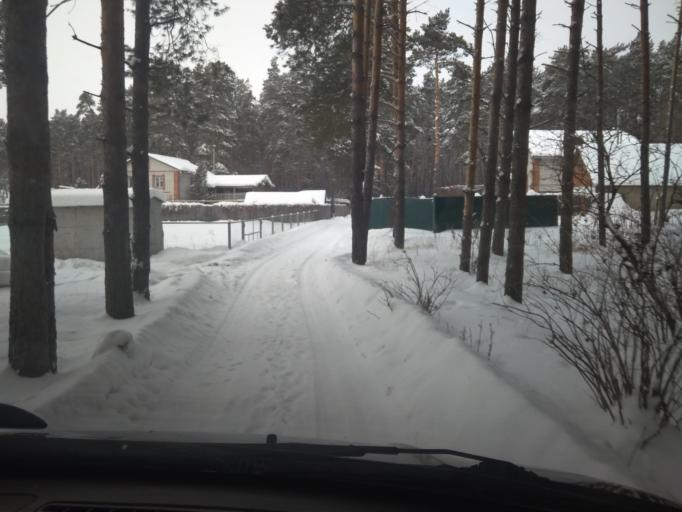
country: RU
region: Mordoviya
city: Kemlya
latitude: 54.7309
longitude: 45.2822
